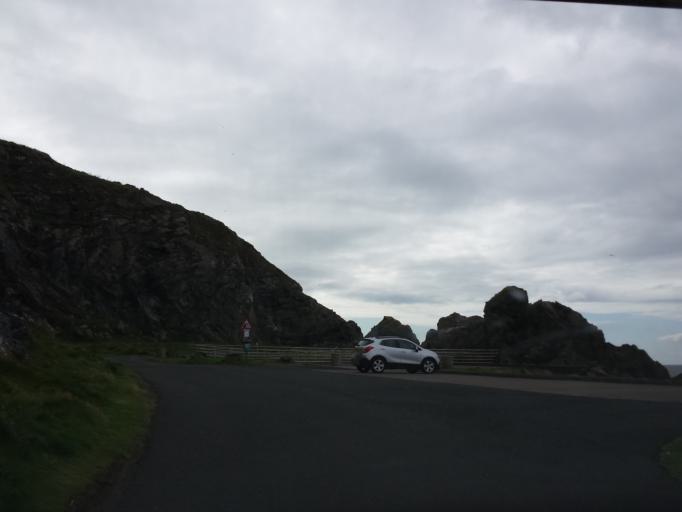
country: GB
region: Scotland
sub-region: Dumfries and Galloway
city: Stranraer
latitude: 54.8388
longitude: -5.1158
